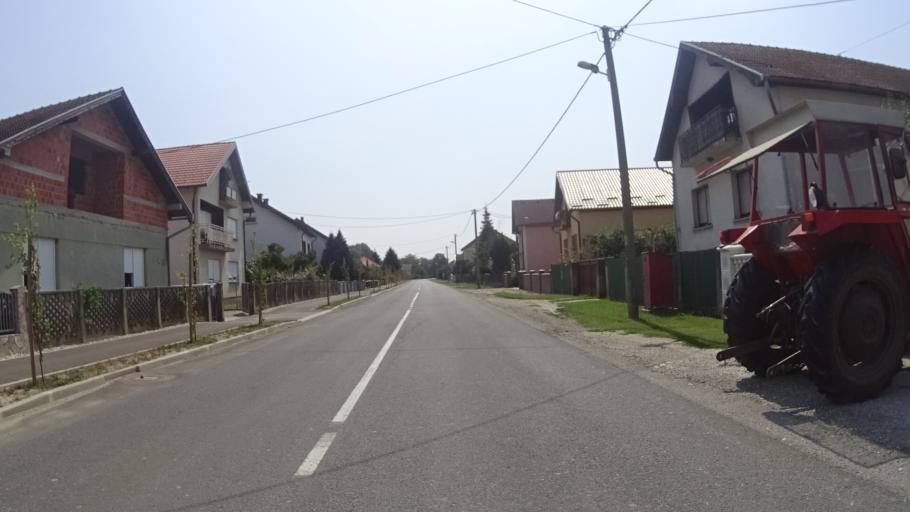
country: HR
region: Medimurska
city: Hodosan
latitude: 46.3998
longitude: 16.6352
